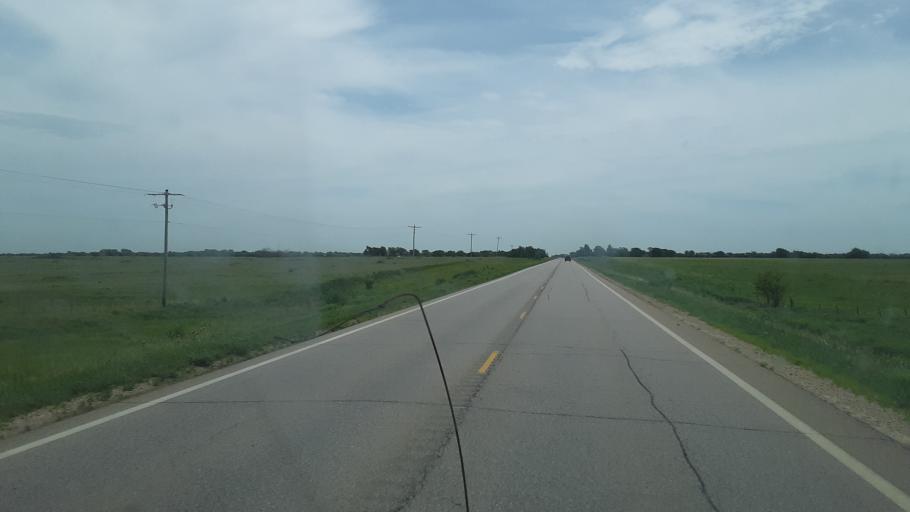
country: US
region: Kansas
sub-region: Butler County
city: El Dorado
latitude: 37.8104
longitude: -96.6971
